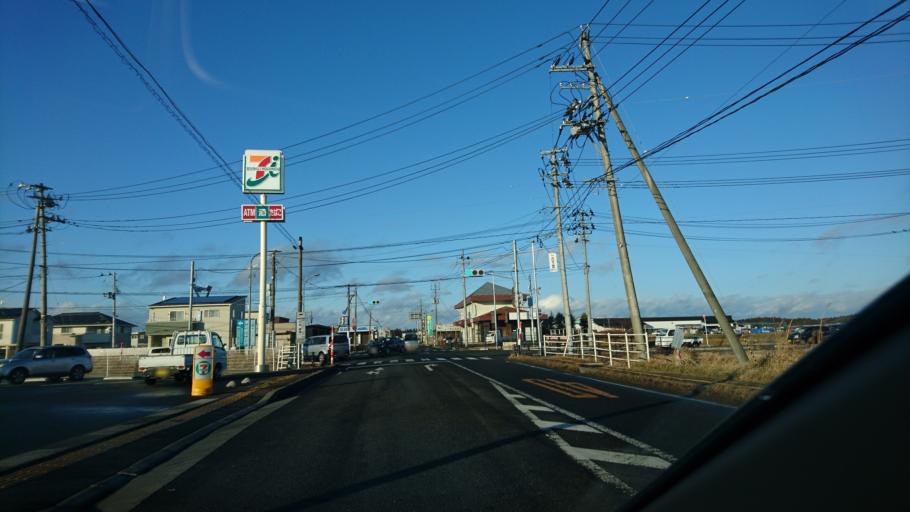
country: JP
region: Miyagi
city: Furukawa
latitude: 38.5763
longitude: 140.8601
